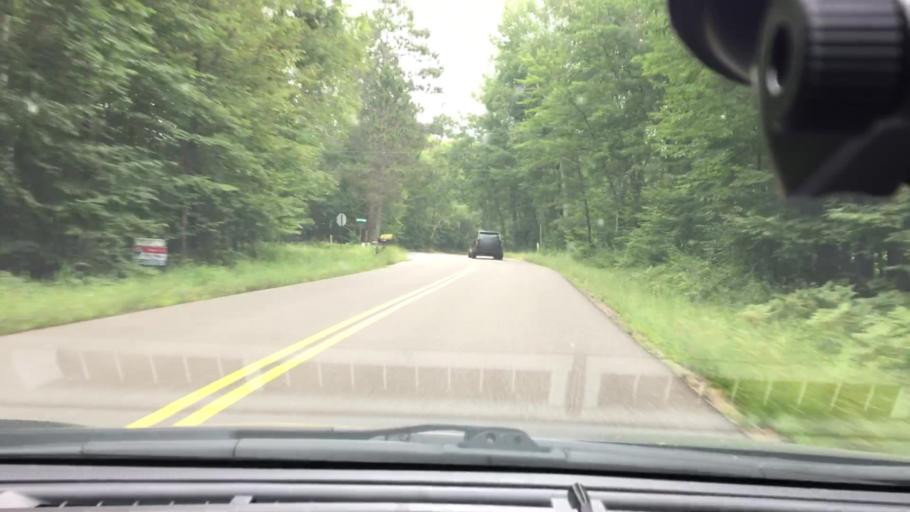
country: US
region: Minnesota
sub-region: Crow Wing County
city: Cross Lake
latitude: 46.6716
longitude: -94.0396
